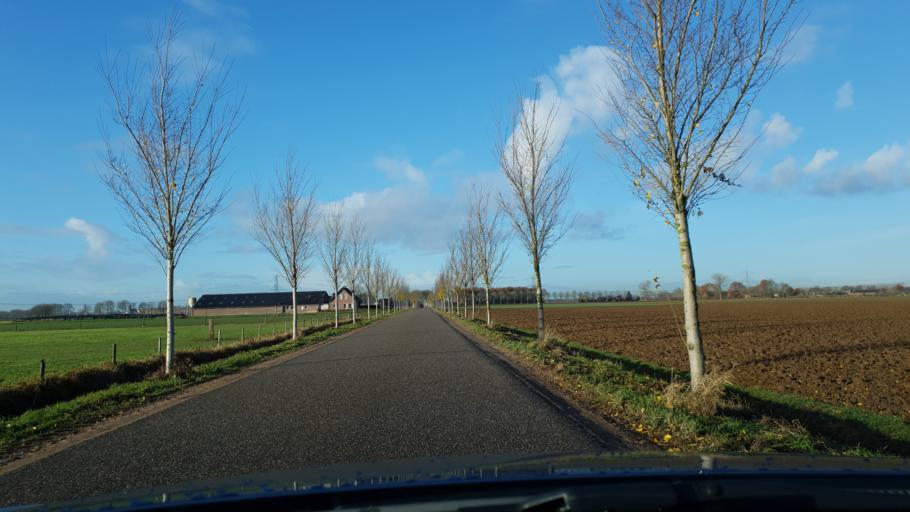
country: NL
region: Gelderland
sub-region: Gemeente Wijchen
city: Bergharen
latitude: 51.8322
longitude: 5.6688
